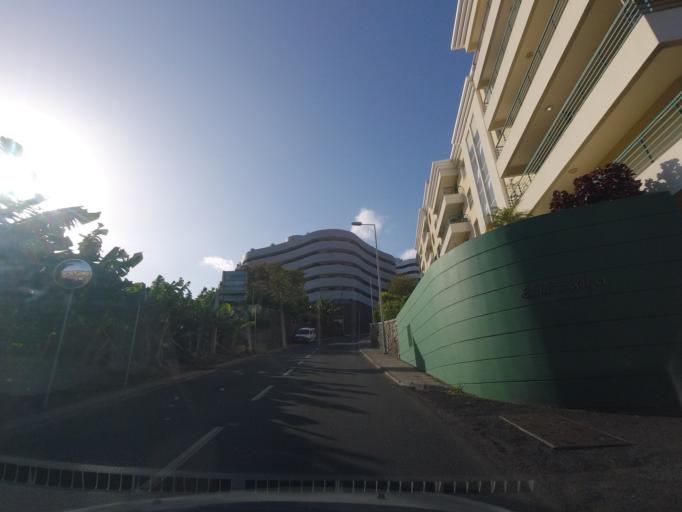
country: PT
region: Madeira
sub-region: Funchal
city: Nossa Senhora do Monte
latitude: 32.6503
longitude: -16.9295
